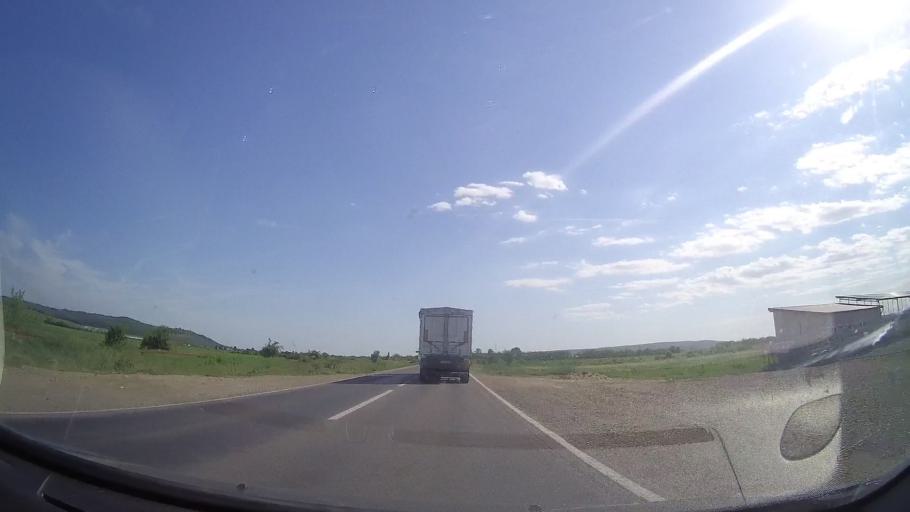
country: RO
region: Prahova
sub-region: Comuna Magurele
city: Magurele
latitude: 45.0776
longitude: 26.0307
